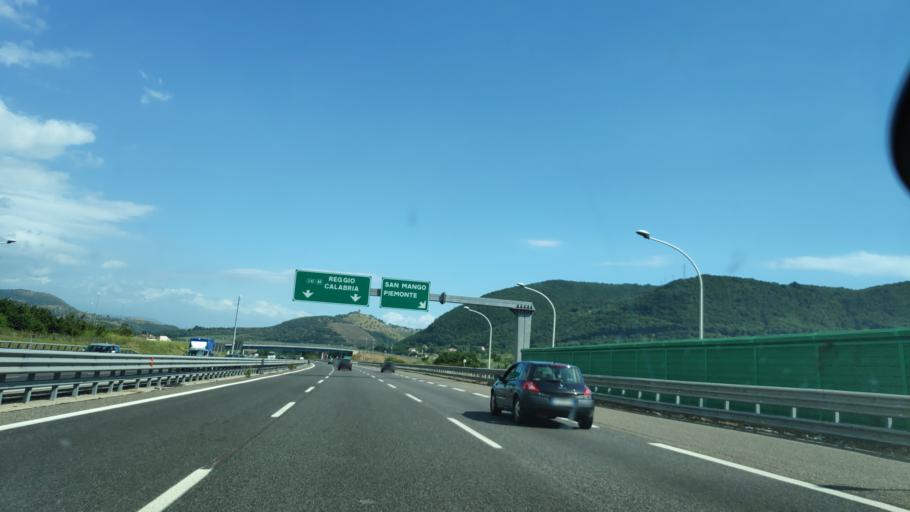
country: IT
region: Campania
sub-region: Provincia di Salerno
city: San Mango Piemonte
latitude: 40.6918
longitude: 14.8358
